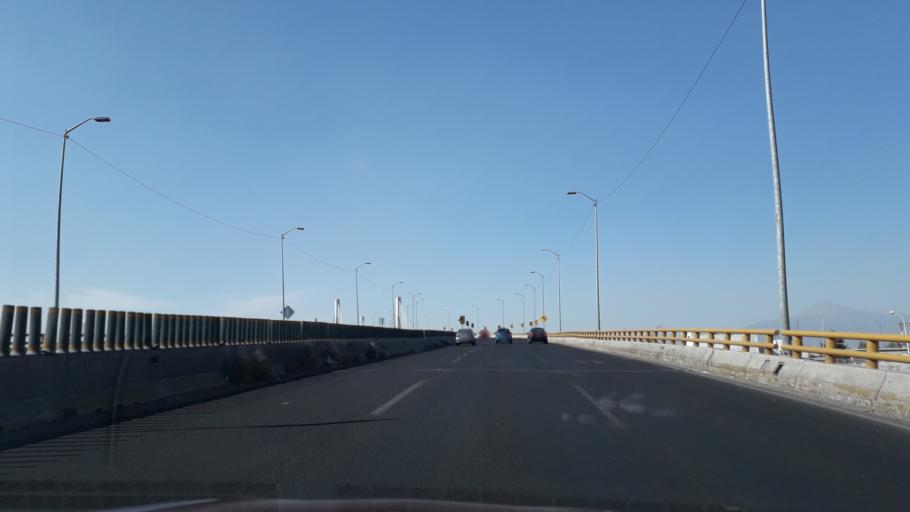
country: MX
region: Puebla
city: Puebla
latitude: 19.0769
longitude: -98.1898
